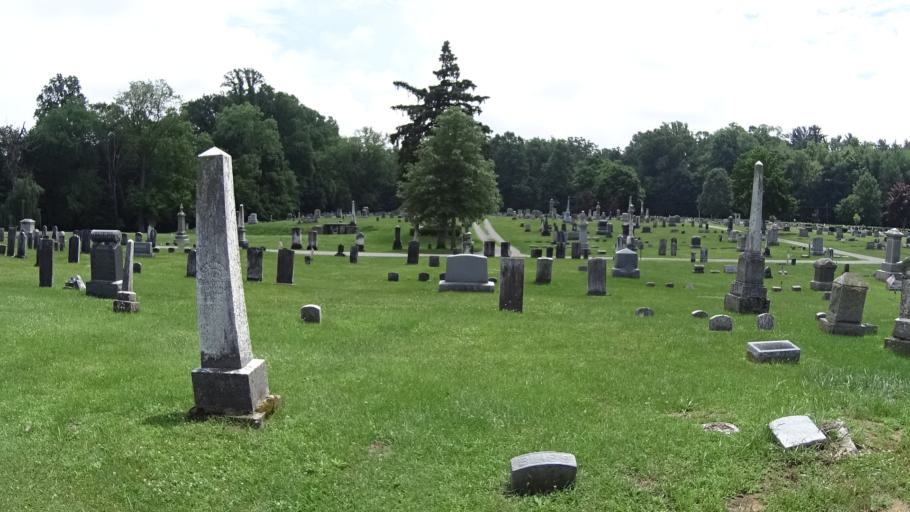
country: US
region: Ohio
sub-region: Erie County
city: Milan
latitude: 41.2938
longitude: -82.5974
